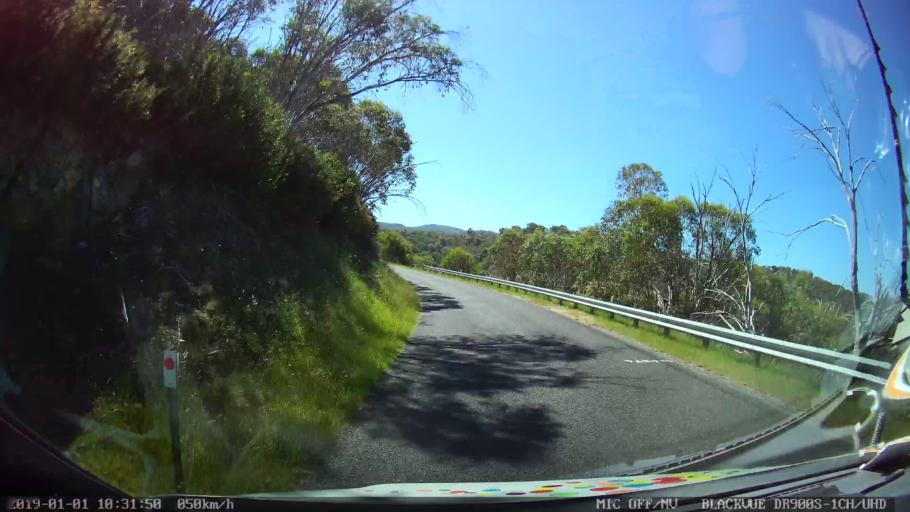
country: AU
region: New South Wales
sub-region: Snowy River
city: Jindabyne
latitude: -36.0557
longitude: 148.2700
